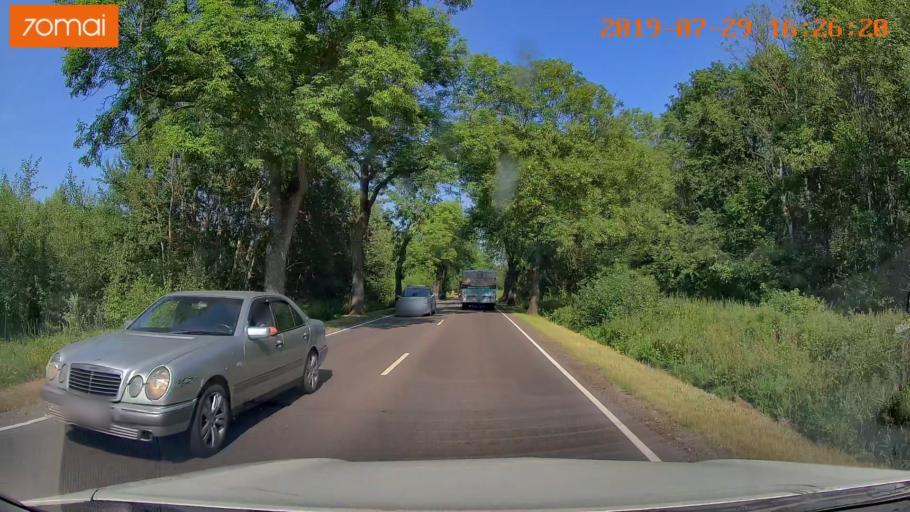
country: RU
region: Kaliningrad
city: Primorsk
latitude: 54.7281
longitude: 19.9764
